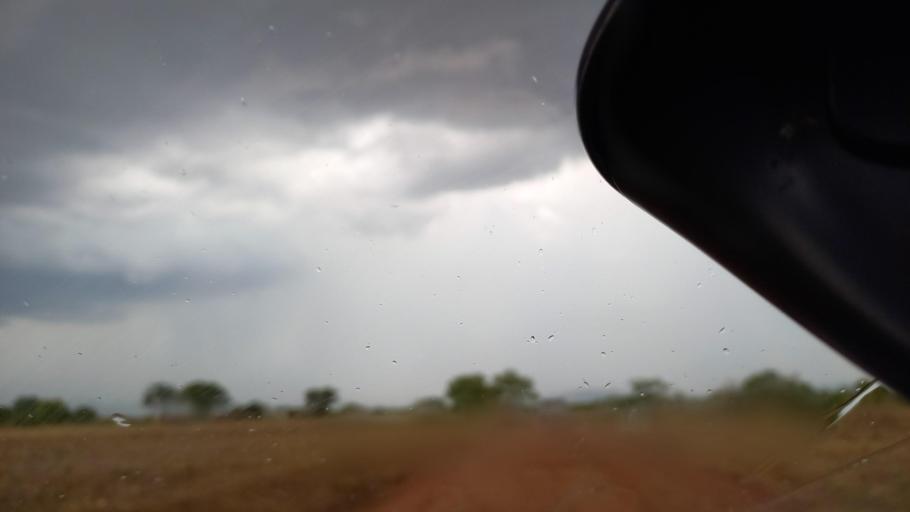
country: ZM
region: Lusaka
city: Kafue
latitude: -15.8661
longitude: 28.1846
